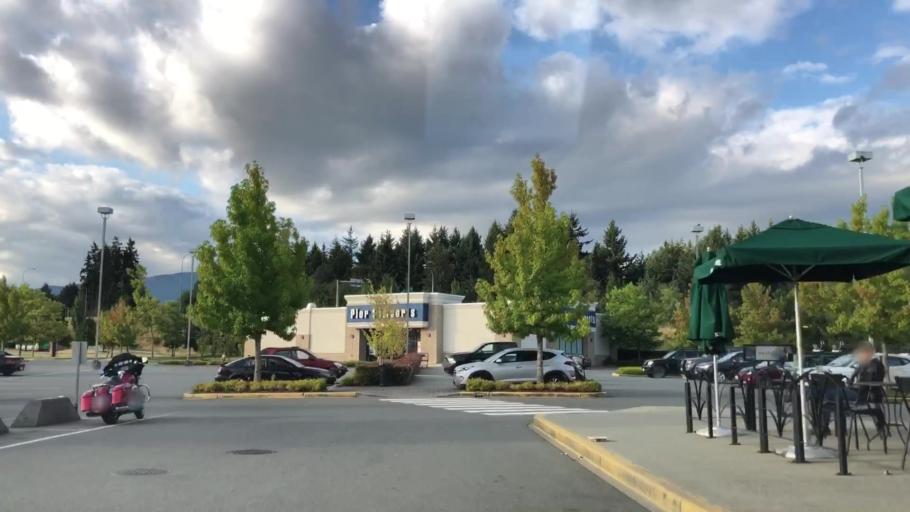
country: CA
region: British Columbia
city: Nanaimo
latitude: 49.2382
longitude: -124.0540
